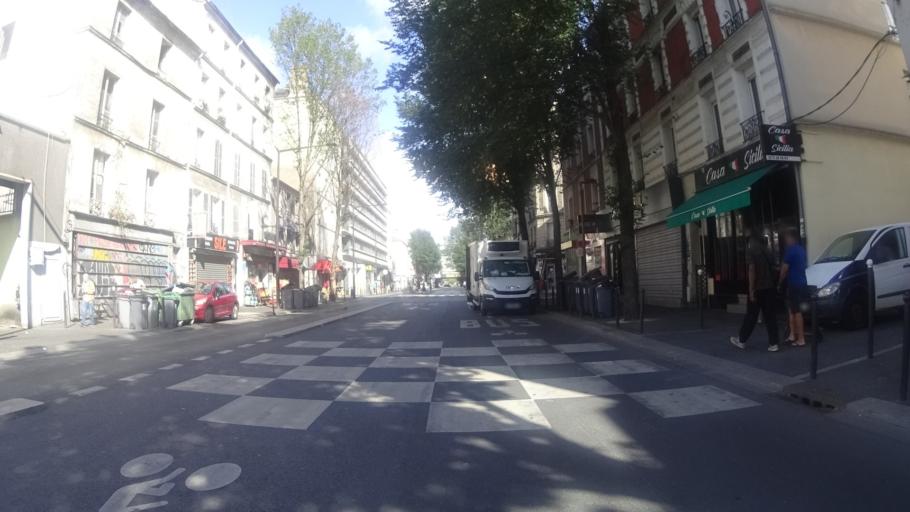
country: FR
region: Ile-de-France
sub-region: Departement du Val-de-Marne
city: Charenton-le-Pont
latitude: 48.8172
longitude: 2.3990
